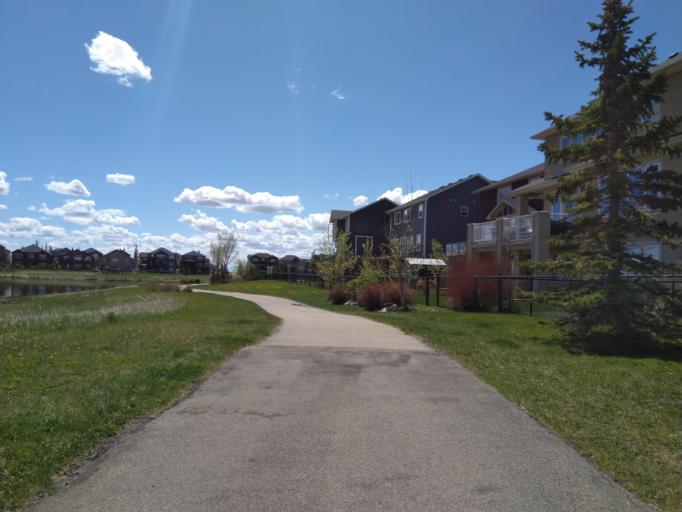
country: CA
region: Alberta
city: Chestermere
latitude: 51.0227
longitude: -113.8346
